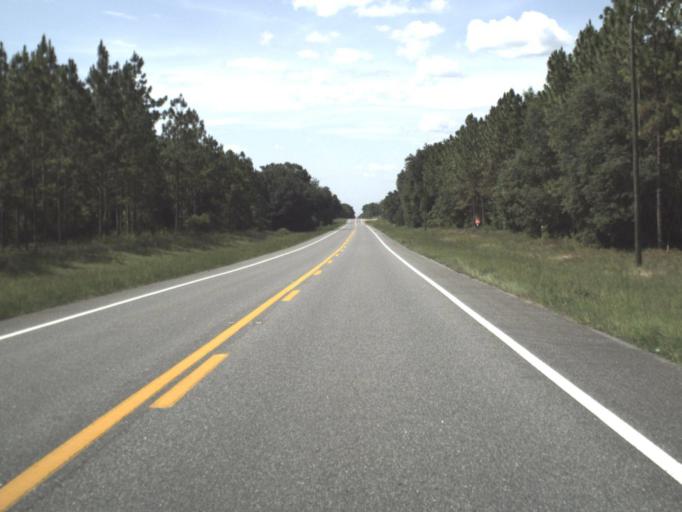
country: US
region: Florida
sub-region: Alachua County
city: High Springs
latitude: 29.7728
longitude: -82.7407
